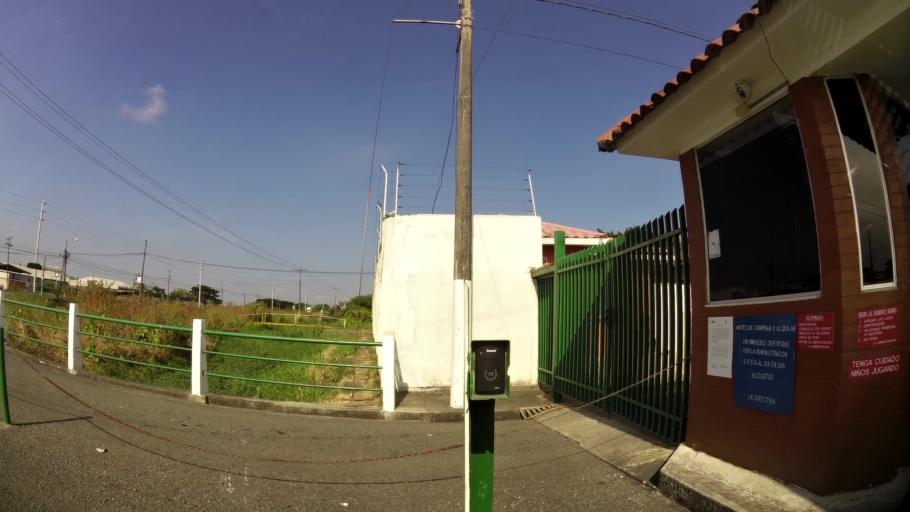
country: EC
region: Guayas
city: Eloy Alfaro
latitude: -2.1892
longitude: -79.8154
